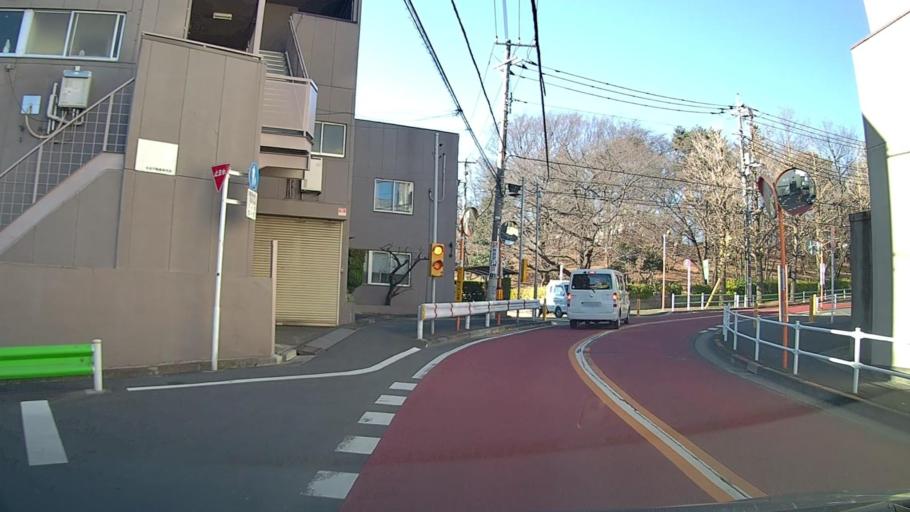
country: JP
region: Tokyo
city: Chofugaoka
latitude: 35.6603
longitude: 139.5632
